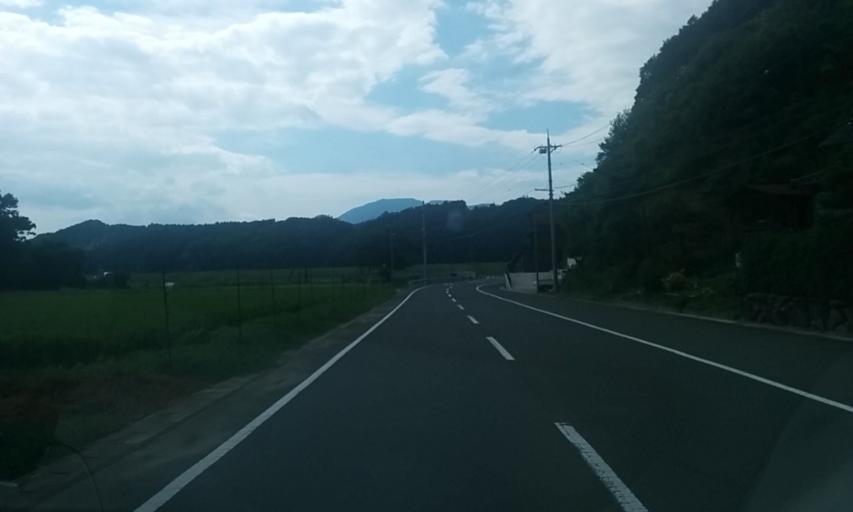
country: JP
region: Kyoto
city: Fukuchiyama
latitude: 35.3766
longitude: 135.1440
